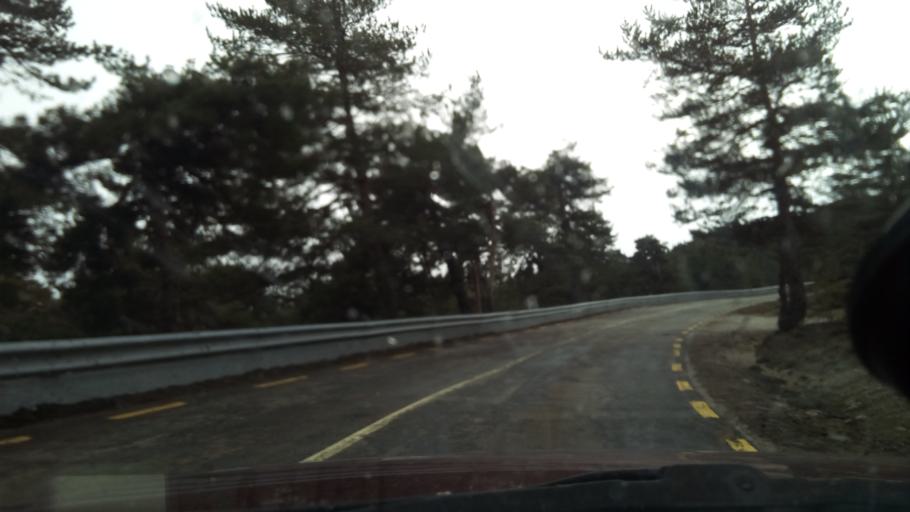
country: PT
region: Guarda
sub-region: Manteigas
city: Manteigas
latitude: 40.4152
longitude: -7.5581
